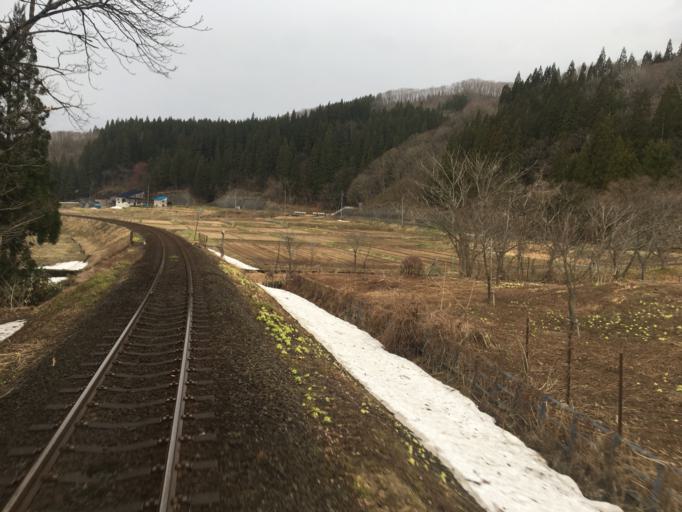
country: JP
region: Akita
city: Takanosu
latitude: 39.9205
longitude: 140.5121
